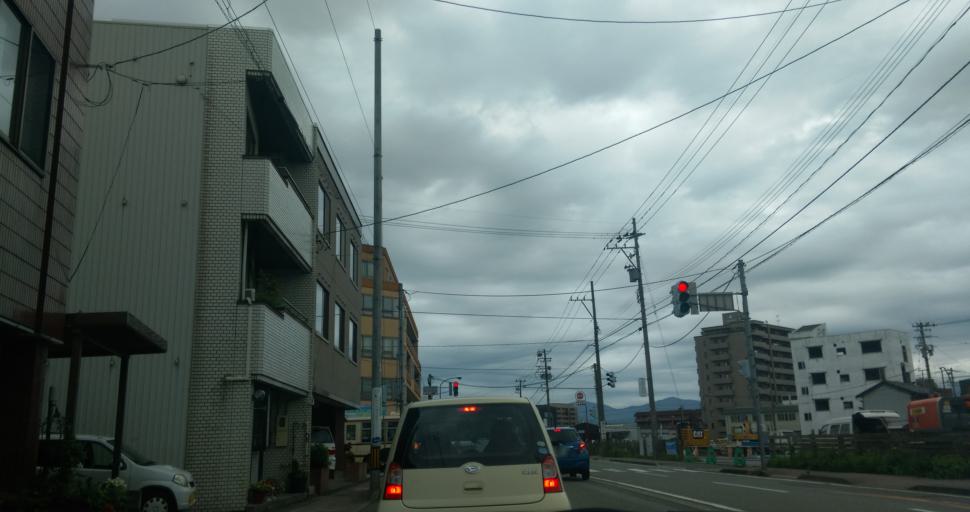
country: JP
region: Fukui
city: Fukui-shi
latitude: 36.0775
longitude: 136.2194
